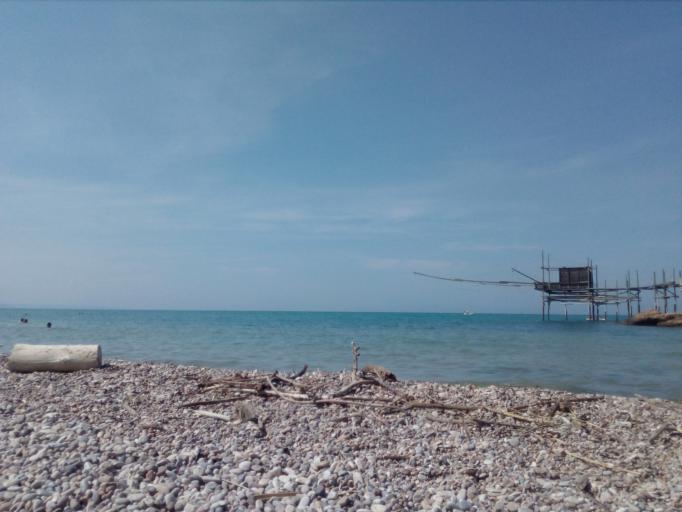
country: IT
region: Abruzzo
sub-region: Provincia di Chieti
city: Vasto
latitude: 42.1801
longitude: 14.6849
